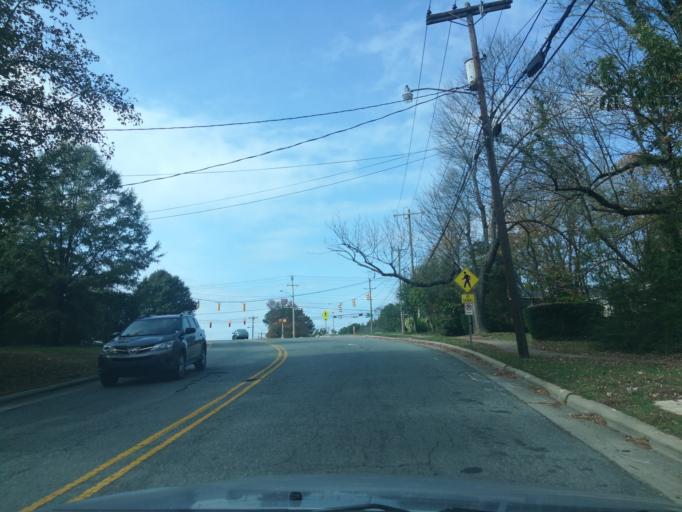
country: US
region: North Carolina
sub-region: Durham County
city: Durham
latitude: 35.9751
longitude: -78.8924
